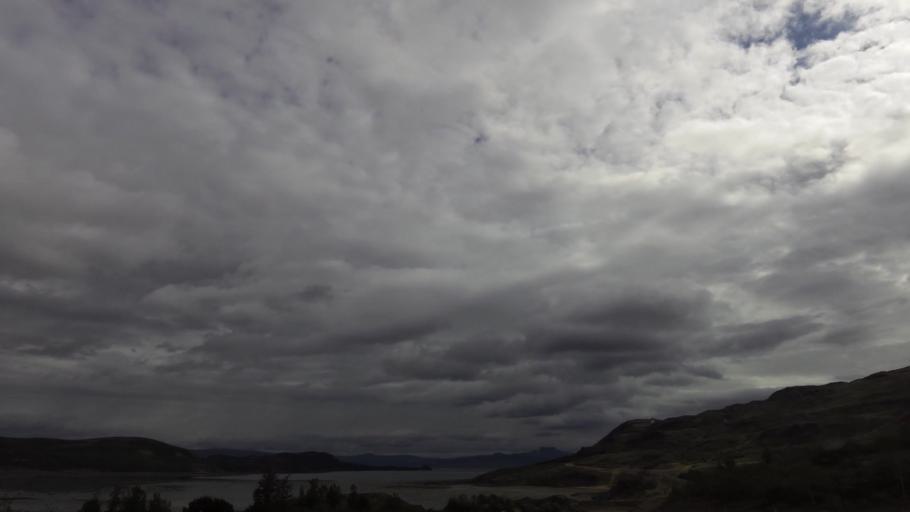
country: IS
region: West
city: Stykkisholmur
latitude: 65.5321
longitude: -22.1223
